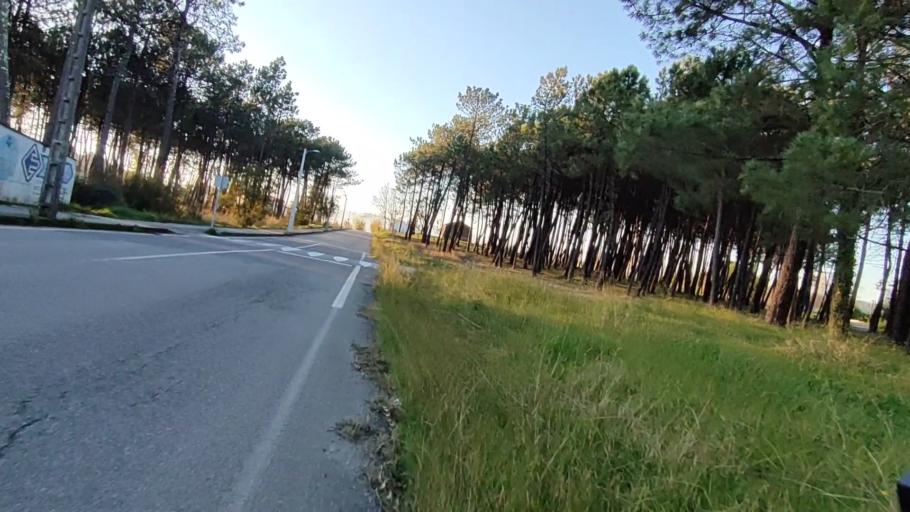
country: ES
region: Galicia
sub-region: Provincia da Coruna
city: Rianxo
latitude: 42.6391
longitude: -8.8568
